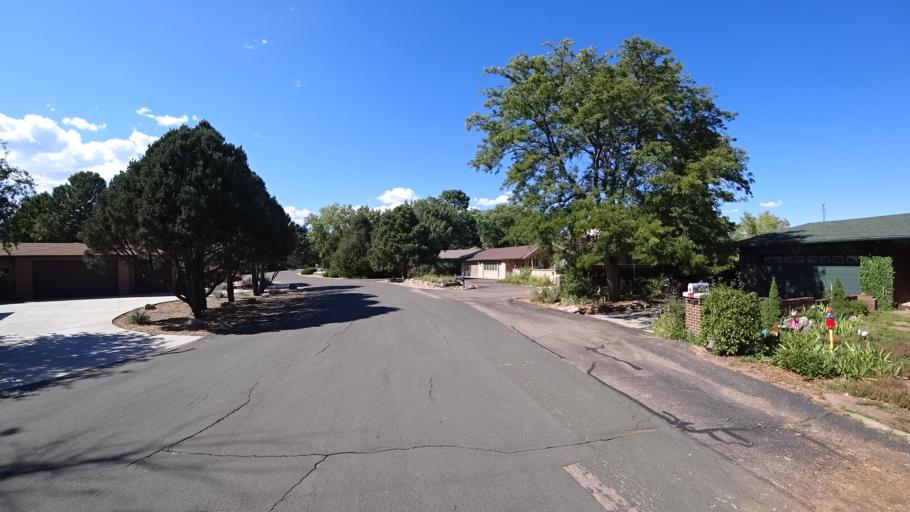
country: US
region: Colorado
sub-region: El Paso County
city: Colorado Springs
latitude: 38.8611
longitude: -104.8566
